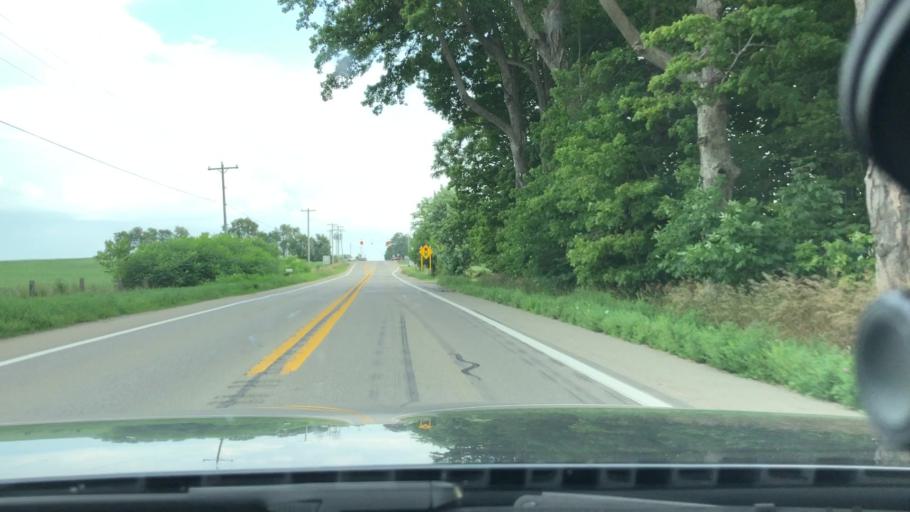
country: US
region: Michigan
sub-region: Washtenaw County
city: Manchester
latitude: 42.1945
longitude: -84.0325
